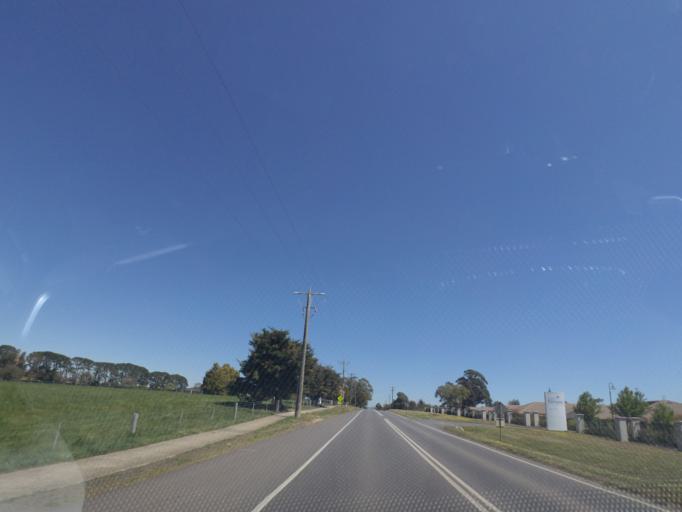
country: AU
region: Victoria
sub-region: Whittlesea
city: Whittlesea
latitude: -37.2954
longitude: 144.9454
